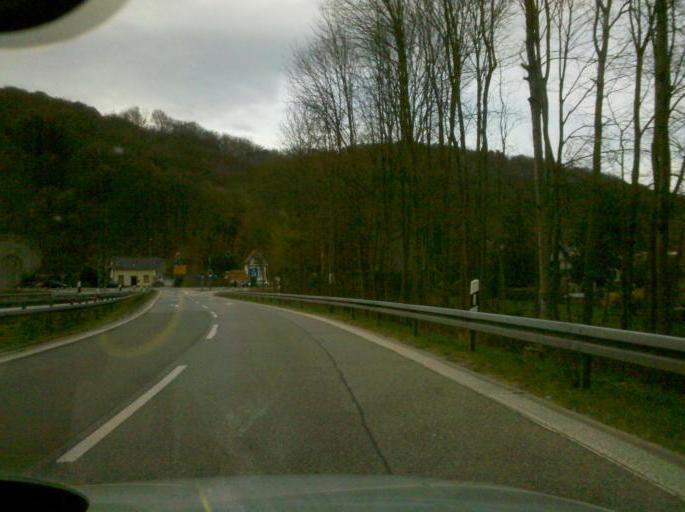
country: DE
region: North Rhine-Westphalia
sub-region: Regierungsbezirk Koln
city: Rosrath
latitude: 50.9496
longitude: 7.2193
